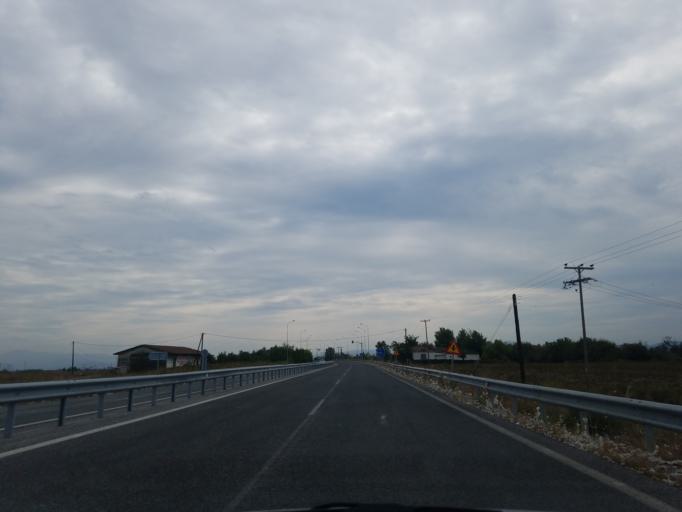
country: GR
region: Thessaly
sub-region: Nomos Kardhitsas
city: Sofades
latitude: 39.3043
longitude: 22.1262
